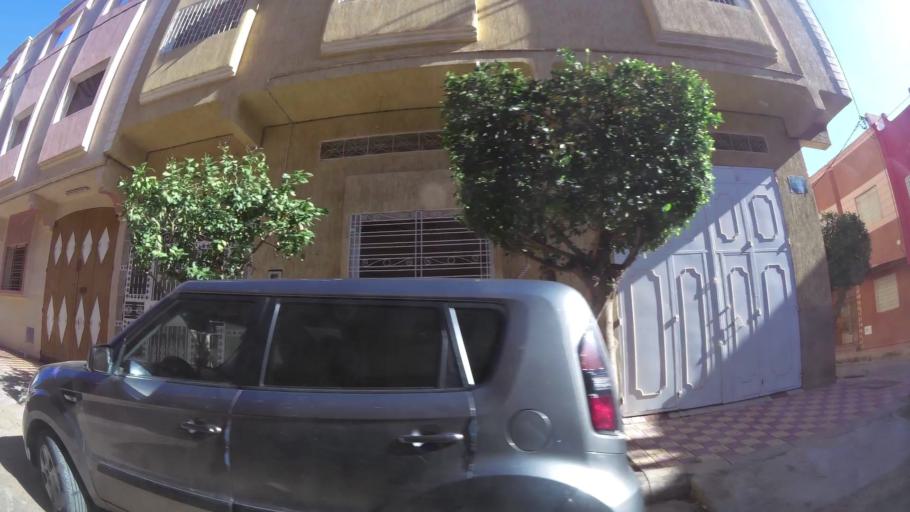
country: MA
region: Oriental
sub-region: Berkane-Taourirt
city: Berkane
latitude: 34.9361
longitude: -2.3334
